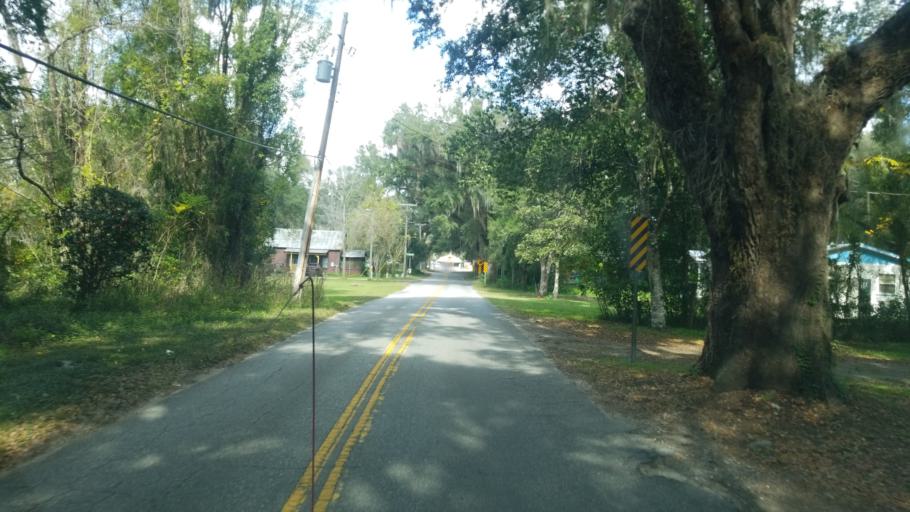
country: US
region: Florida
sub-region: Citrus County
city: Floral City
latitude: 28.7478
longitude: -82.2960
